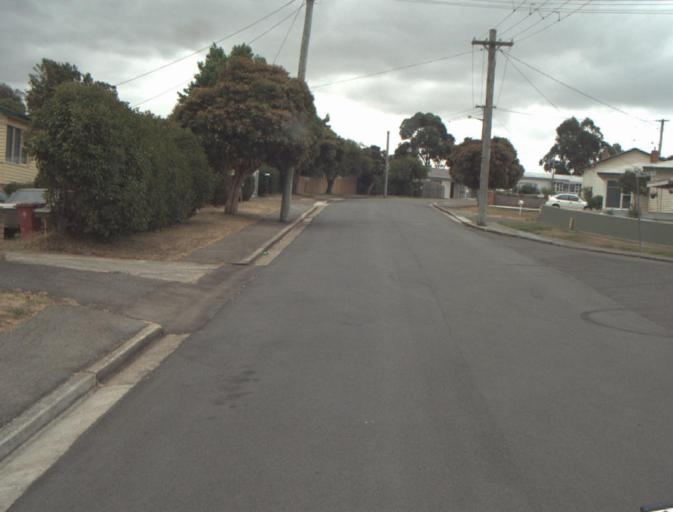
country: AU
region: Tasmania
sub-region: Launceston
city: Newstead
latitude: -41.4329
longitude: 147.1841
